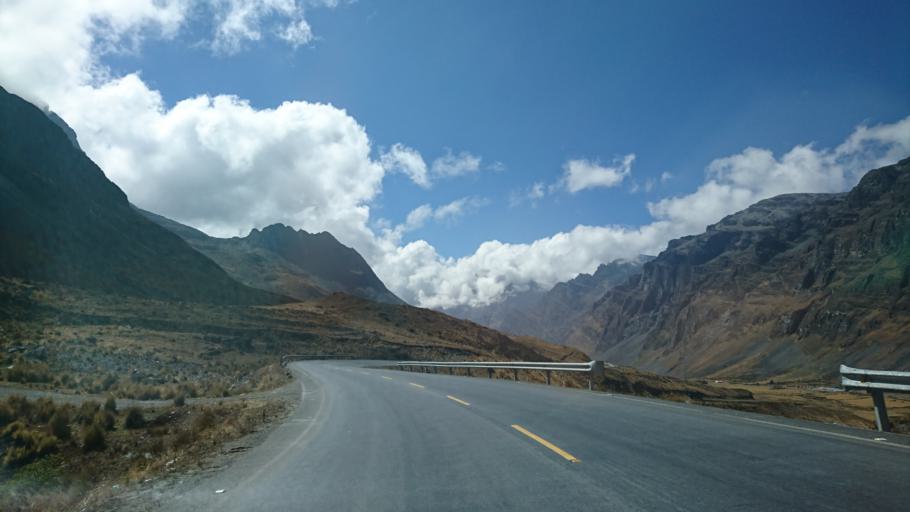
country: BO
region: La Paz
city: La Paz
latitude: -16.3190
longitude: -68.0215
